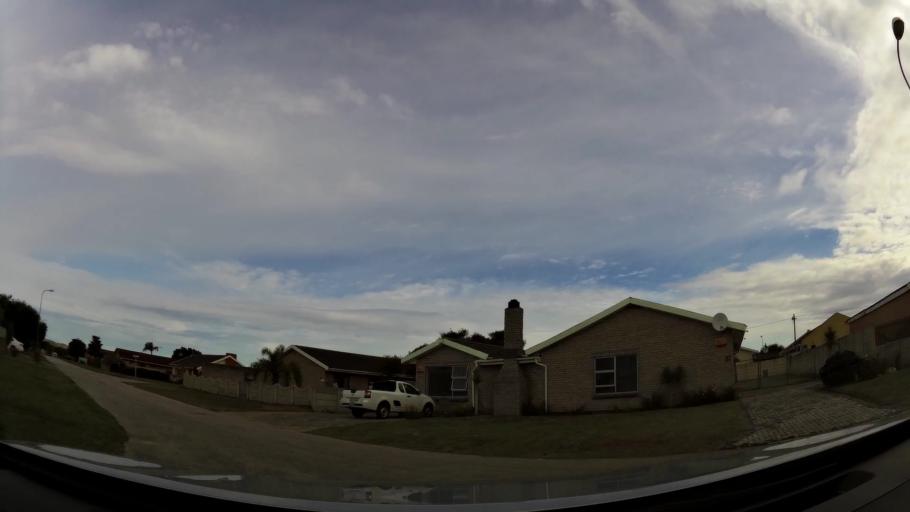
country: ZA
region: Eastern Cape
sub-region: Nelson Mandela Bay Metropolitan Municipality
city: Port Elizabeth
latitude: -33.9384
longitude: 25.4646
